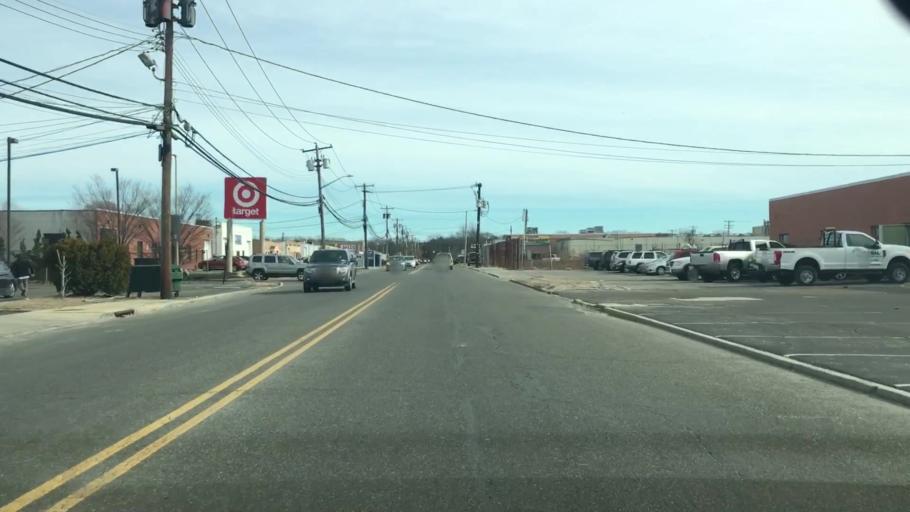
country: US
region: New York
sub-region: Suffolk County
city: East Farmingdale
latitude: 40.7501
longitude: -73.4201
